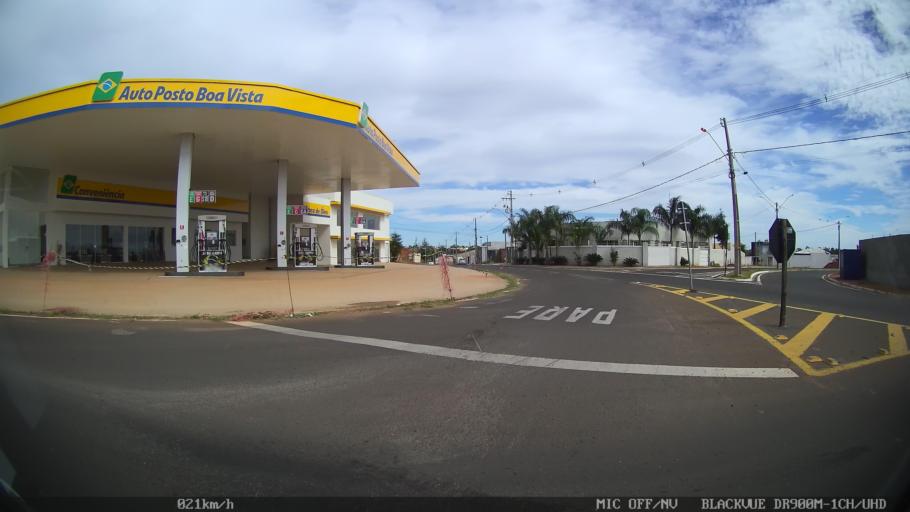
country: BR
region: Sao Paulo
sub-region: Catanduva
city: Catanduva
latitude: -21.1603
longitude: -48.9630
